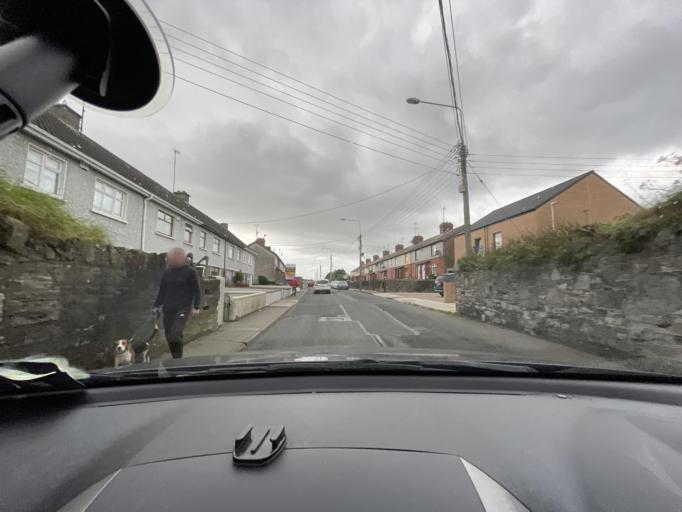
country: IE
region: Leinster
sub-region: Lu
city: Drogheda
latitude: 53.7199
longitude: -6.3376
